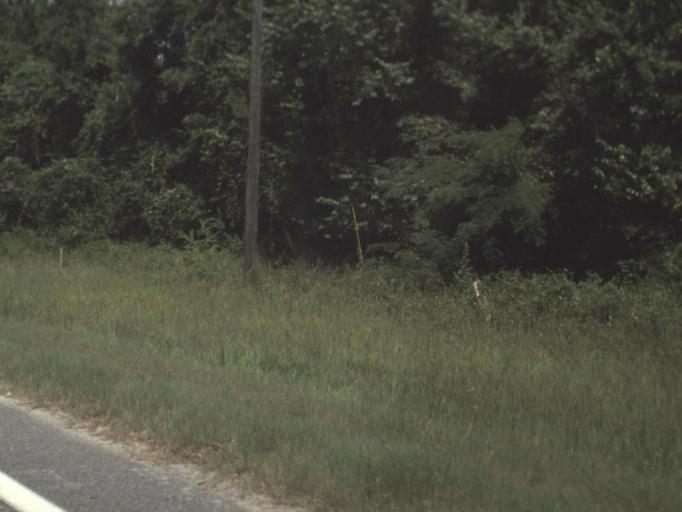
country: US
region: Florida
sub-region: Hamilton County
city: Jasper
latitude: 30.5281
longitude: -83.0485
